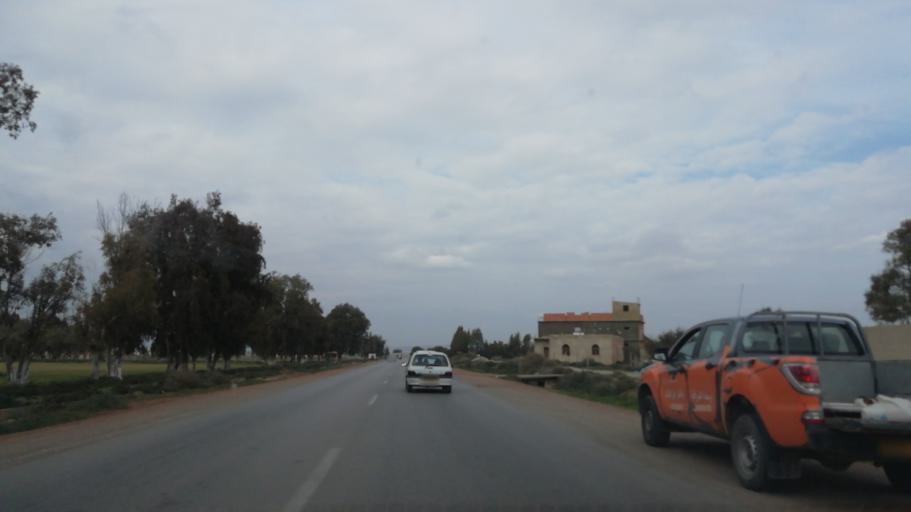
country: DZ
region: Mostaganem
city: Mostaganem
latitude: 35.6838
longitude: 0.0566
